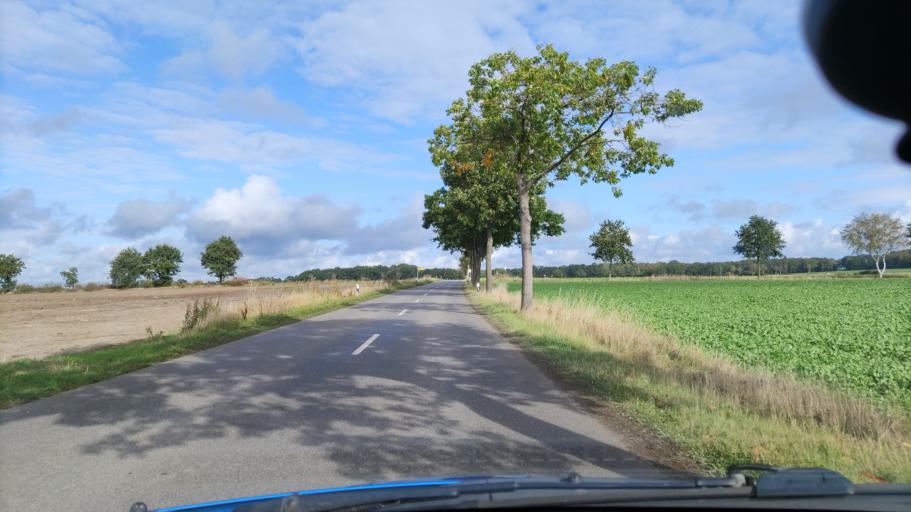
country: DE
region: Lower Saxony
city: Romstedt
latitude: 53.0850
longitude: 10.6720
